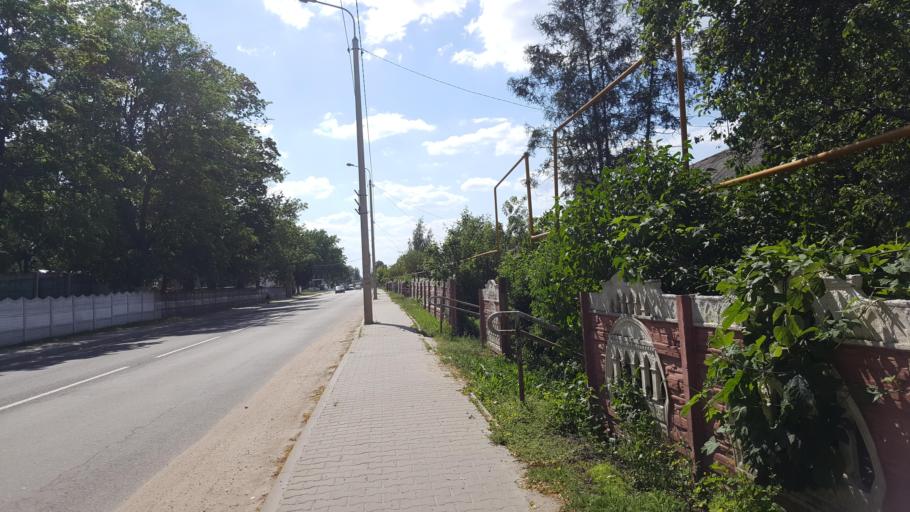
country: BY
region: Brest
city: Horad Kobryn
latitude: 52.2135
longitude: 24.3752
